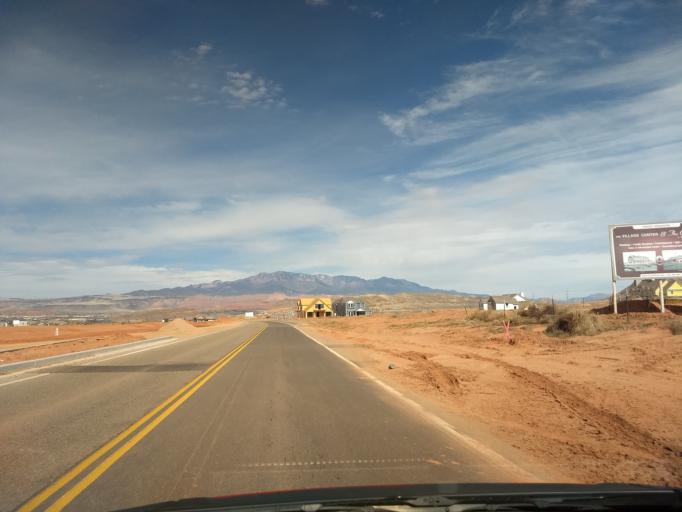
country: US
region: Utah
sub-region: Washington County
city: Washington
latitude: 37.0620
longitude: -113.4902
